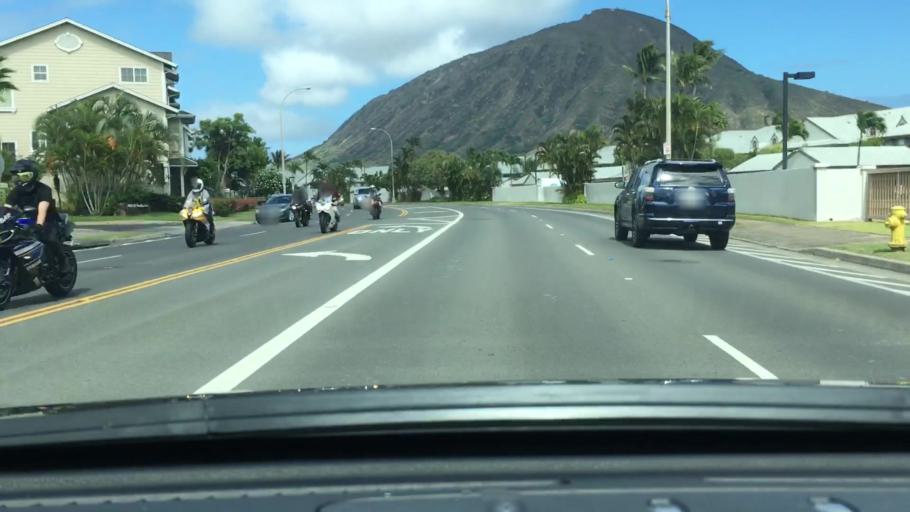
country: US
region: Hawaii
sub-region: Honolulu County
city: Waimanalo Beach
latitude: 21.2868
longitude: -157.7044
